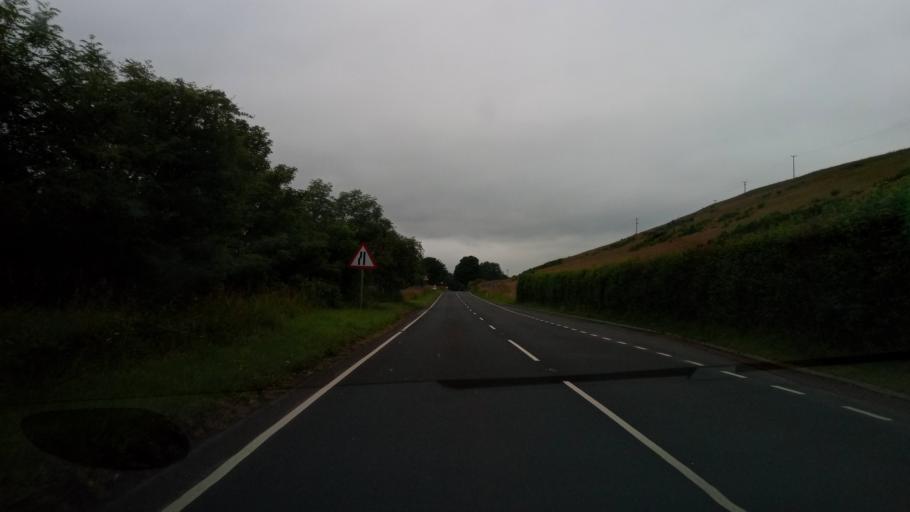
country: GB
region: Scotland
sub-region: The Scottish Borders
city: Hawick
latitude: 55.3810
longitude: -2.8705
